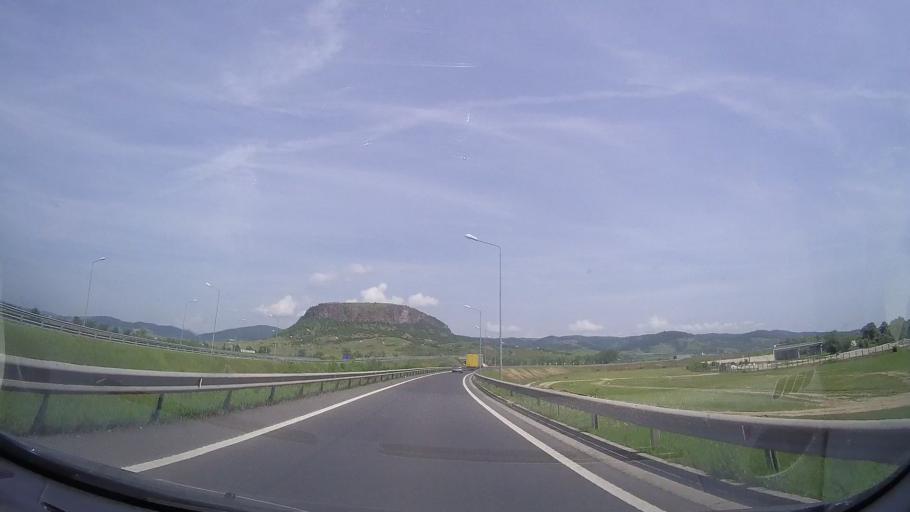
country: RO
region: Hunedoara
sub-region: Oras Simeria
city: Simeria
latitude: 45.8459
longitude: 23.0441
